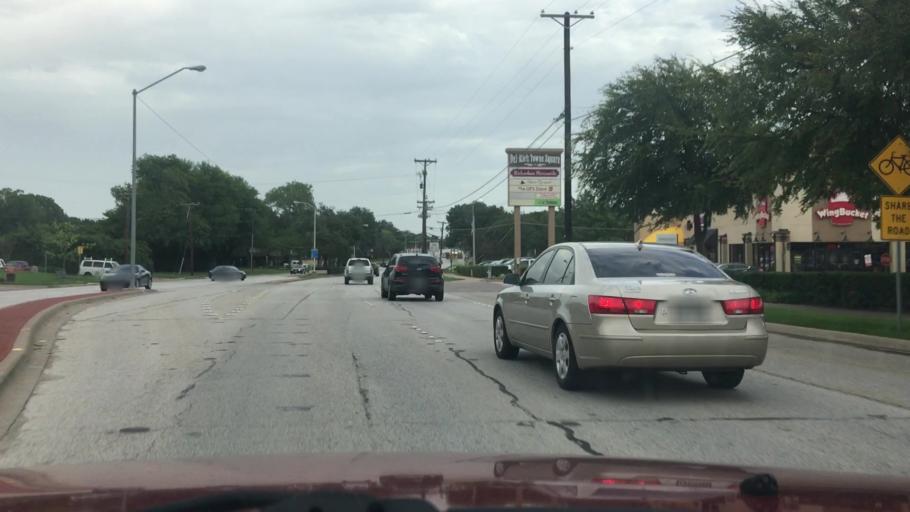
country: US
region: Texas
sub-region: Dallas County
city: Richardson
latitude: 32.9510
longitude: -96.7683
